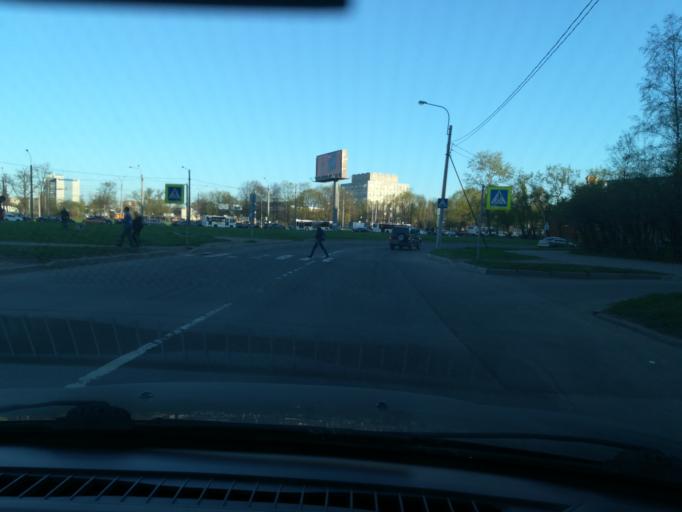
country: RU
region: St.-Petersburg
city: Avtovo
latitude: 59.8615
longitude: 30.2553
